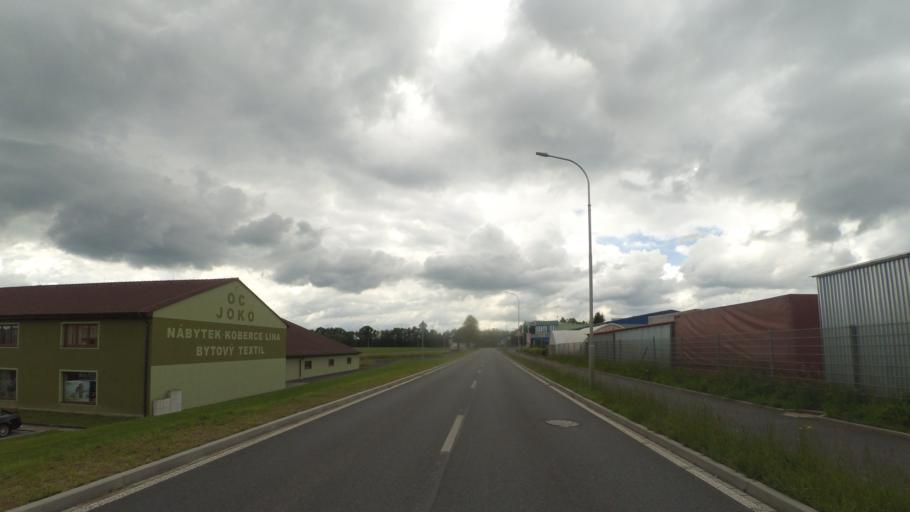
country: CZ
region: Plzensky
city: Horsovsky Tyn
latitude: 49.5341
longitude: 12.9293
